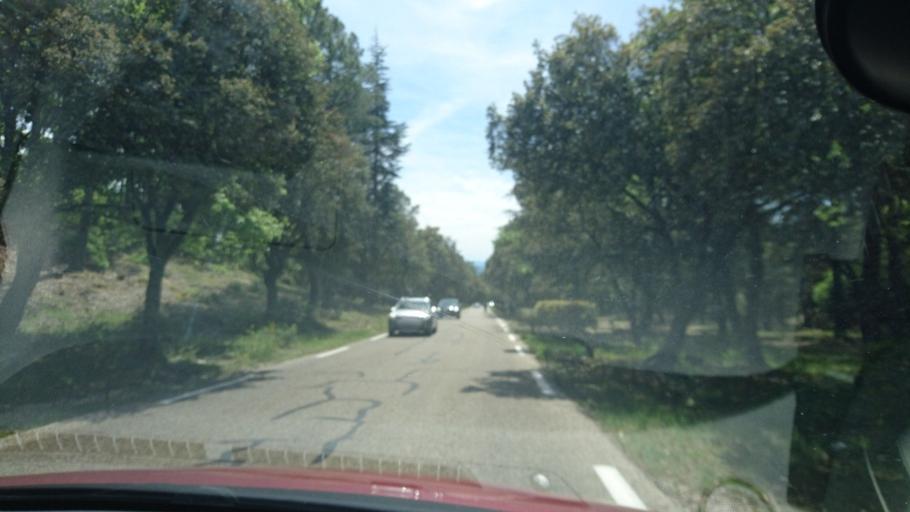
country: FR
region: Provence-Alpes-Cote d'Azur
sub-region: Departement du Vaucluse
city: Villes-sur-Auzon
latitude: 44.1170
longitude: 5.2464
